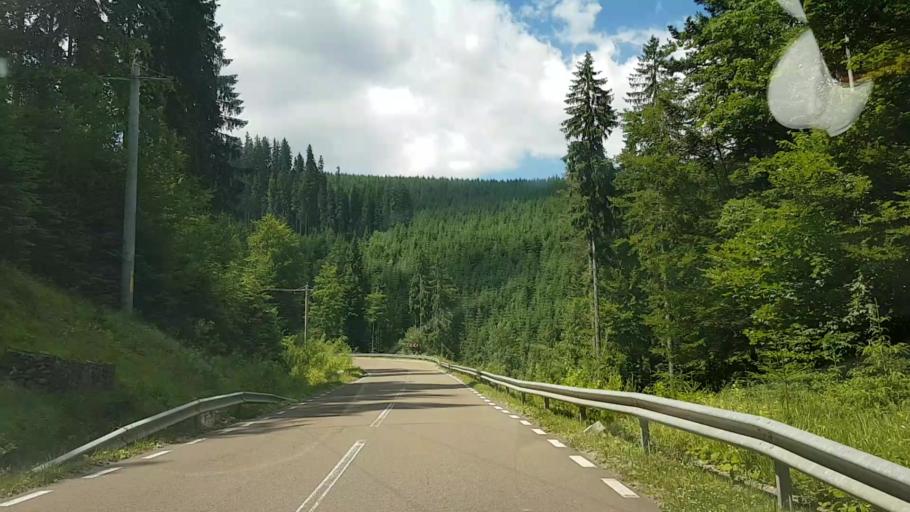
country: RO
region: Suceava
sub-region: Comuna Sadova
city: Sadova
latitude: 47.4632
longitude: 25.5137
